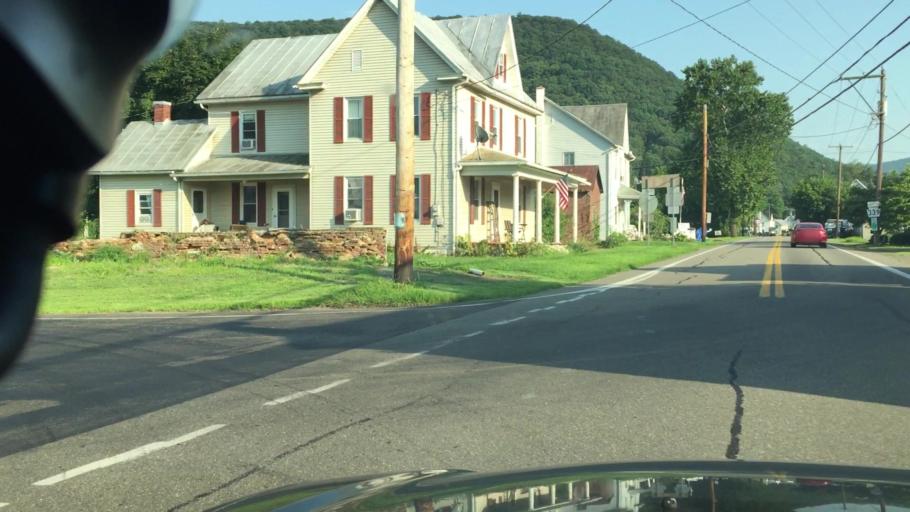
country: US
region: Pennsylvania
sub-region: Columbia County
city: Almedia
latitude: 40.9758
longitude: -76.3742
